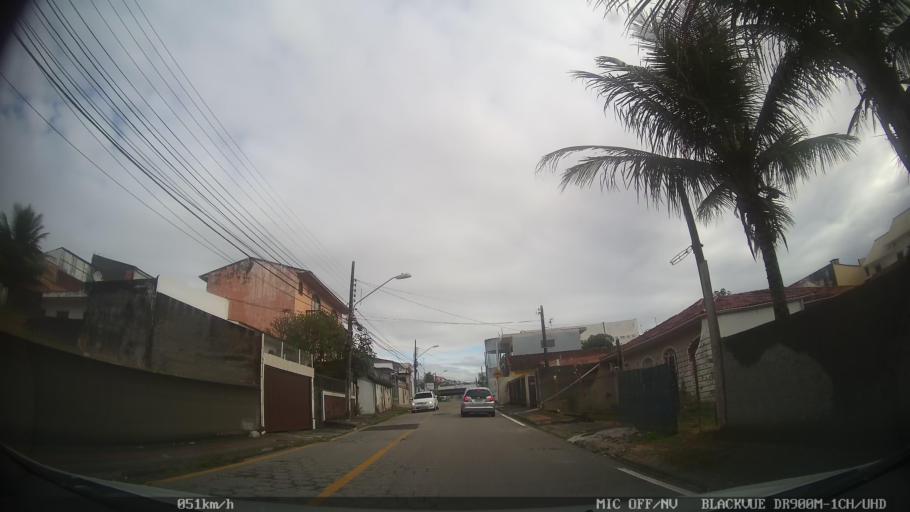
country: BR
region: Santa Catarina
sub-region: Sao Jose
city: Campinas
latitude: -27.5728
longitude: -48.6127
